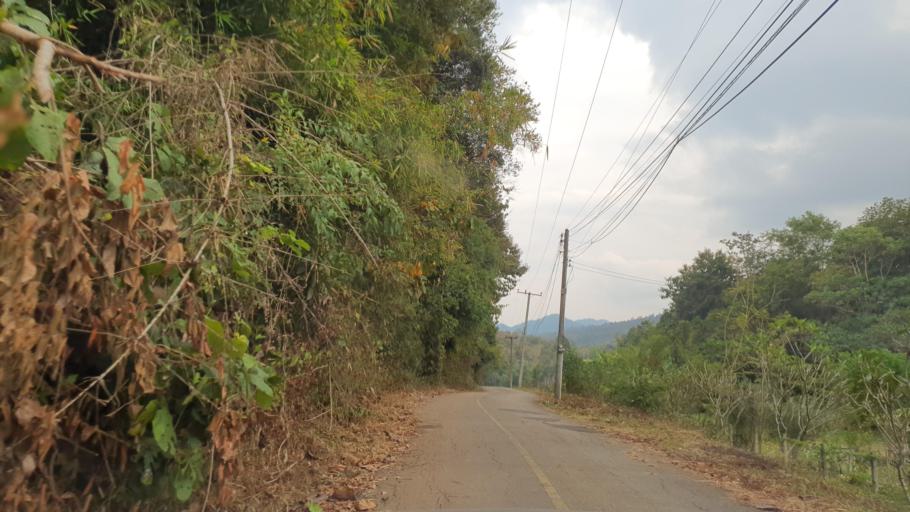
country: TH
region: Chiang Mai
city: Mae Wang
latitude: 18.6609
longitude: 98.6390
